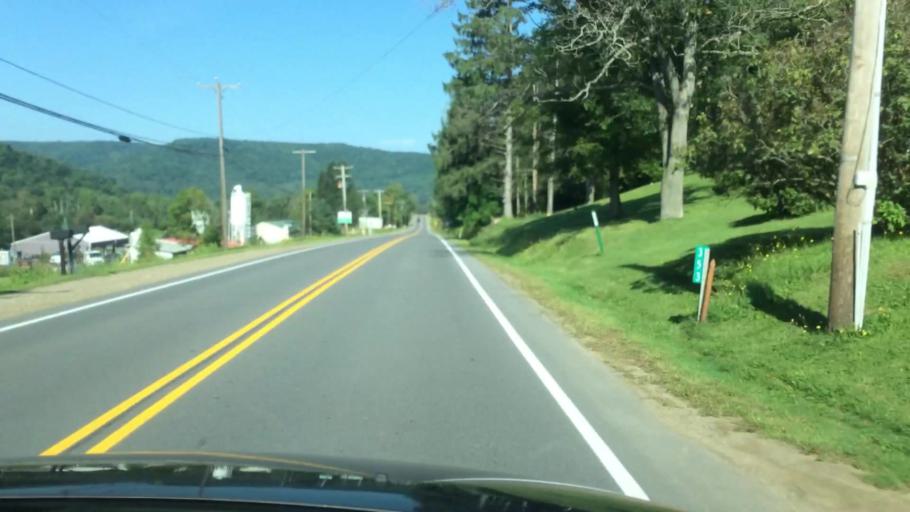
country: US
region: Pennsylvania
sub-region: McKean County
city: Bradford
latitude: 41.9076
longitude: -78.6247
